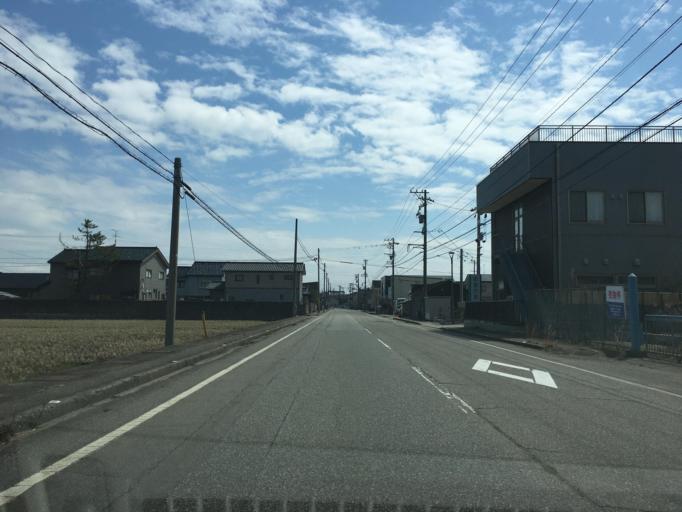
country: JP
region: Toyama
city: Nishishinminato
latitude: 36.7998
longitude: 137.0549
